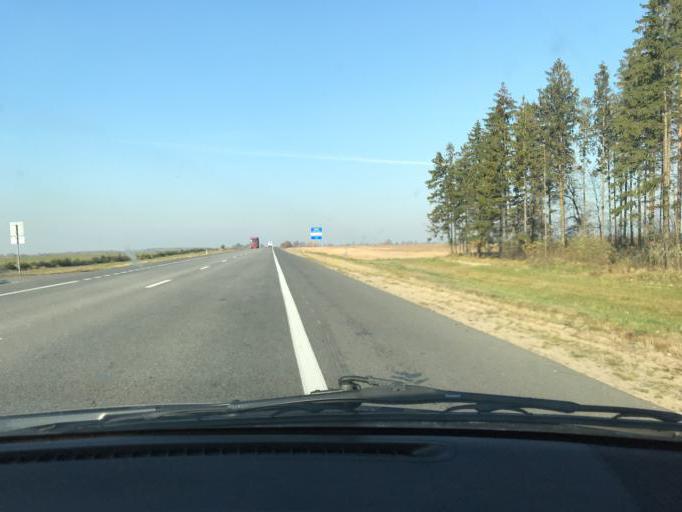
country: BY
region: Mogilev
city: Shklow
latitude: 54.3005
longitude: 30.4483
